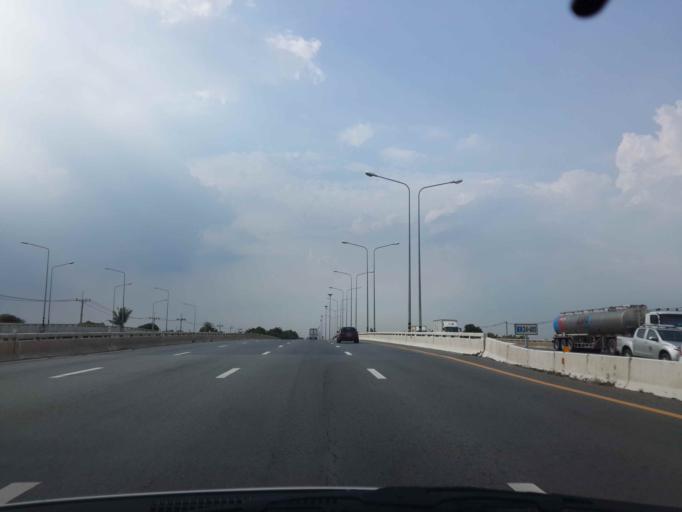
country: TH
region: Samut Prakan
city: Ban Khlong Bang Sao Thong
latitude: 13.6813
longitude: 100.8342
